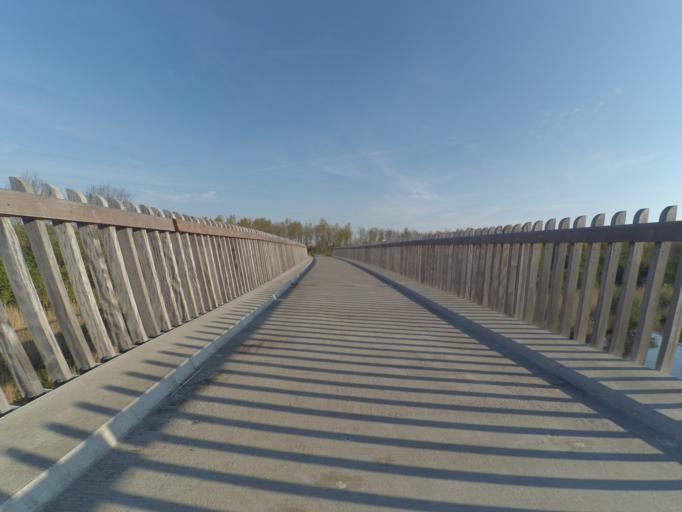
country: NL
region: Flevoland
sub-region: Gemeente Almere
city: Almere Stad
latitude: 52.4107
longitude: 5.3589
